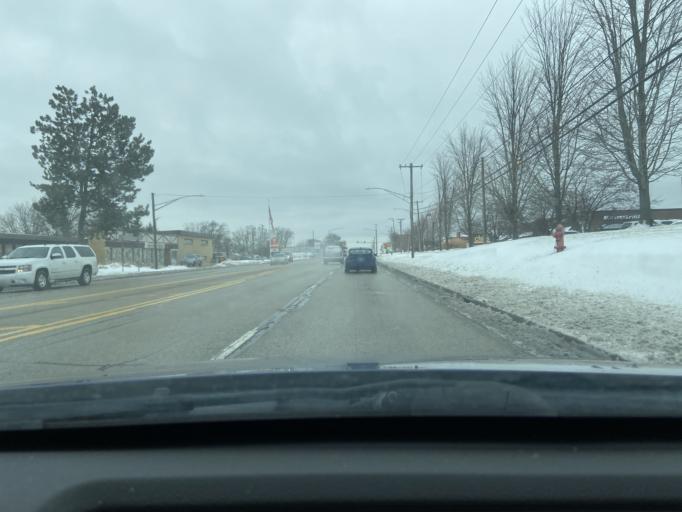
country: US
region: Illinois
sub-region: Lake County
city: Round Lake Beach
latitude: 42.3789
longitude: -88.0746
